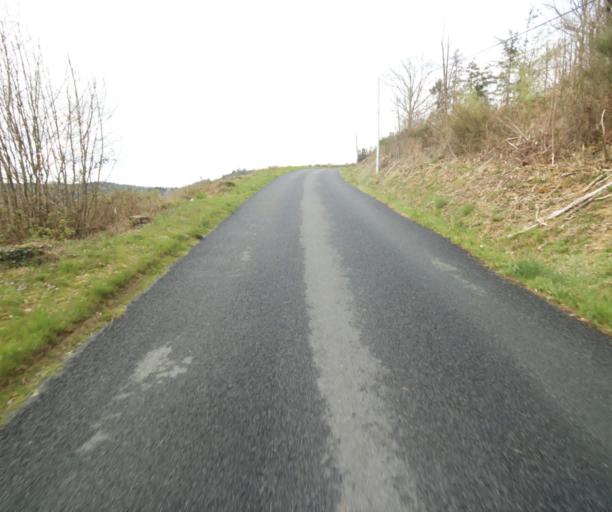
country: FR
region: Limousin
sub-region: Departement de la Correze
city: Tulle
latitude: 45.2659
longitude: 1.7490
